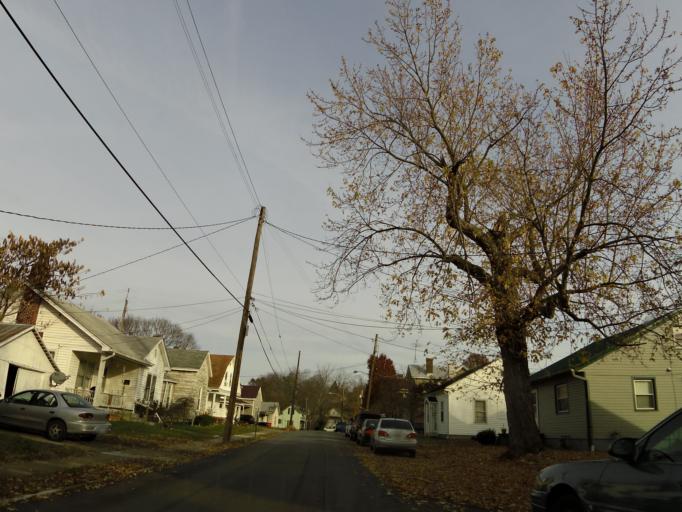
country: US
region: Kentucky
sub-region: Harrison County
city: Cynthiana
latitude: 38.3914
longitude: -84.2912
